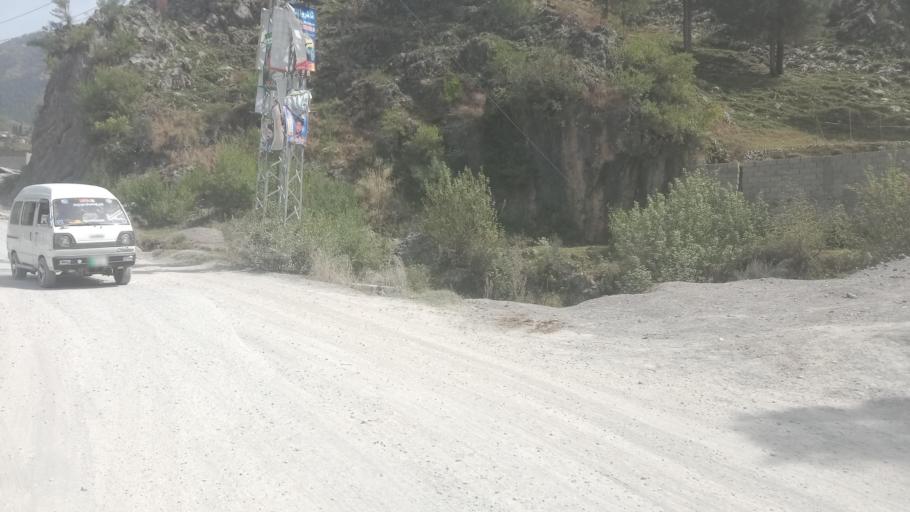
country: PK
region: Khyber Pakhtunkhwa
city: Abbottabad
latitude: 34.1618
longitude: 73.2782
